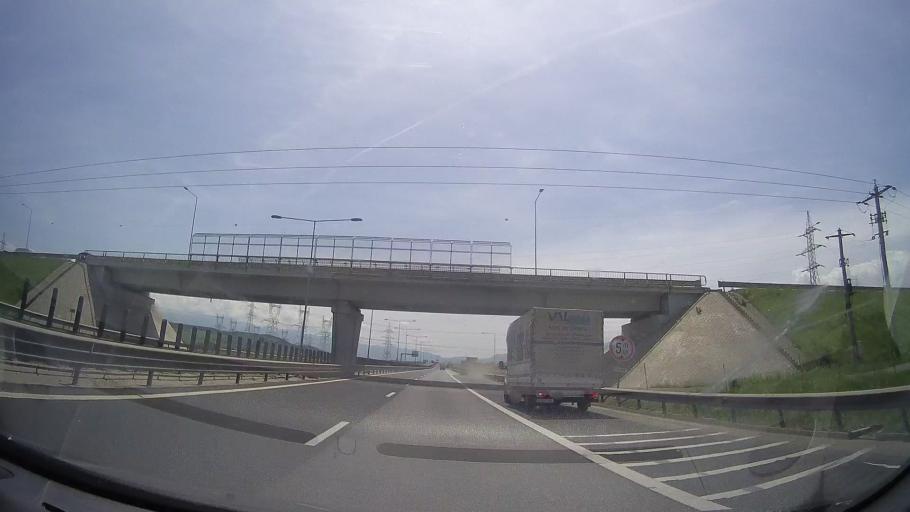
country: RO
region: Sibiu
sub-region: Comuna Selimbar
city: Selimbar
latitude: 45.7895
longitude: 24.1989
